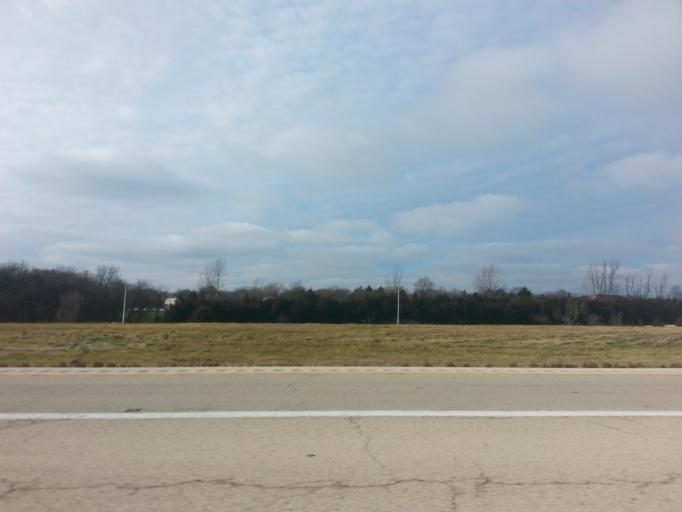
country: US
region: Illinois
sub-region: Winnebago County
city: Cherry Valley
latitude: 42.2125
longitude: -89.0113
